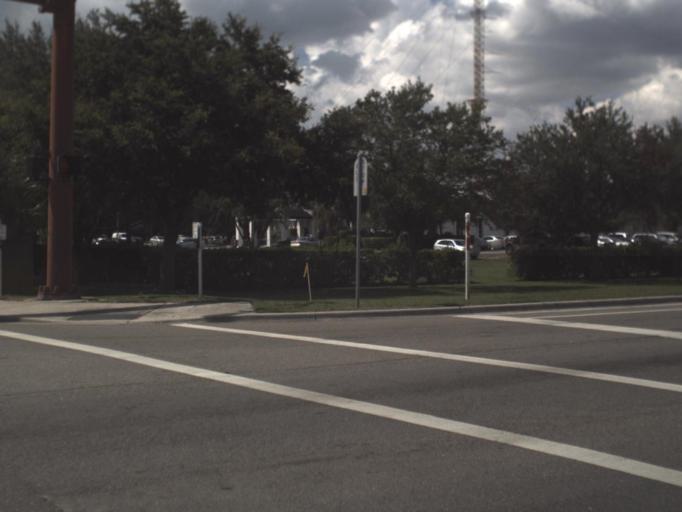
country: US
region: Florida
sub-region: Sarasota County
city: Fruitville
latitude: 27.3380
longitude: -82.4638
